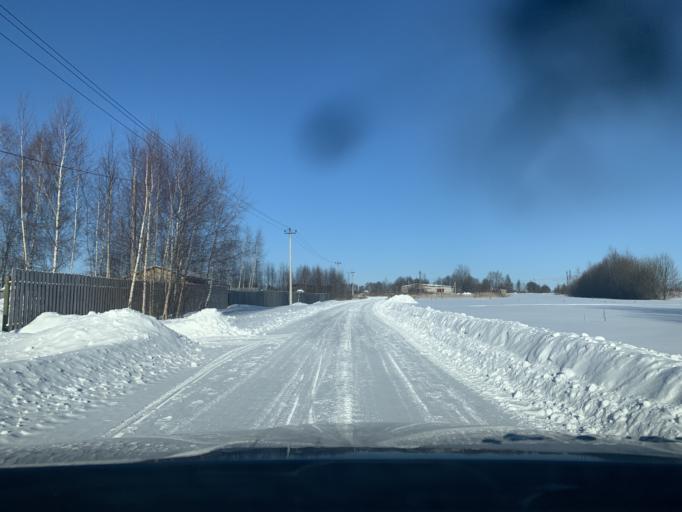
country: RU
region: Jaroslavl
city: Tunoshna
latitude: 57.6517
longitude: 40.0678
